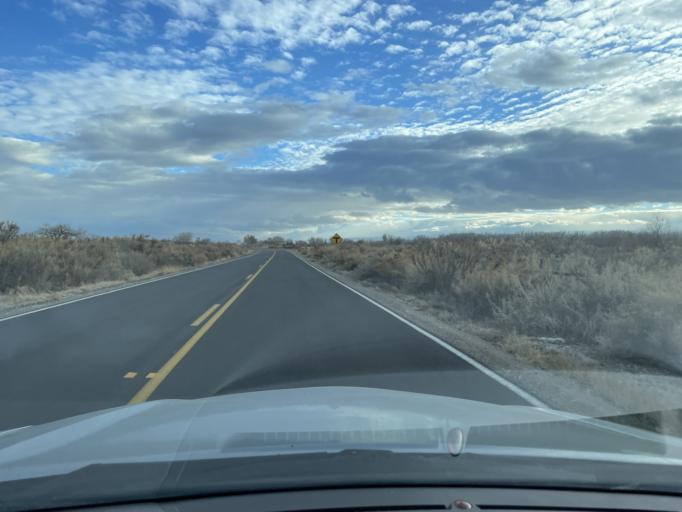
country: US
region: Colorado
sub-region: Montrose County
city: Olathe
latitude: 38.6441
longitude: -107.9939
